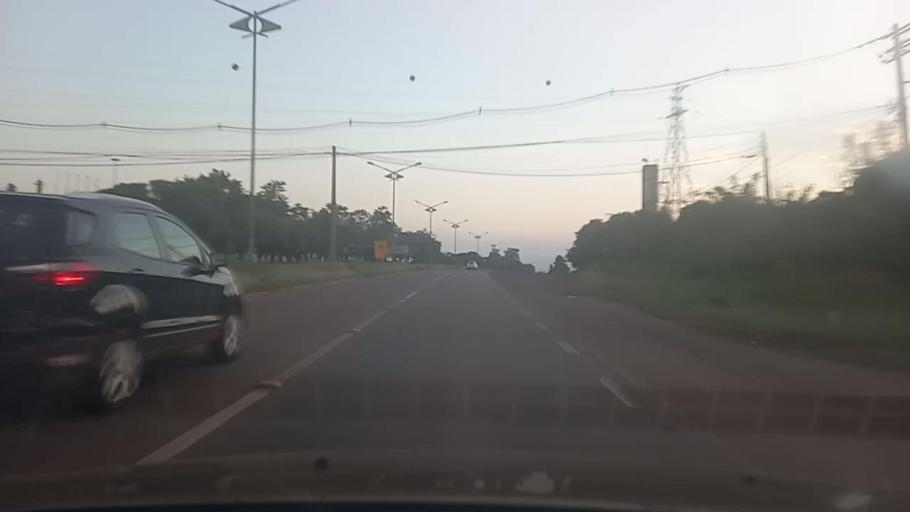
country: BR
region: Rio Grande do Sul
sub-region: Passo Fundo
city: Passo Fundo
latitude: -28.2796
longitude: -52.4507
